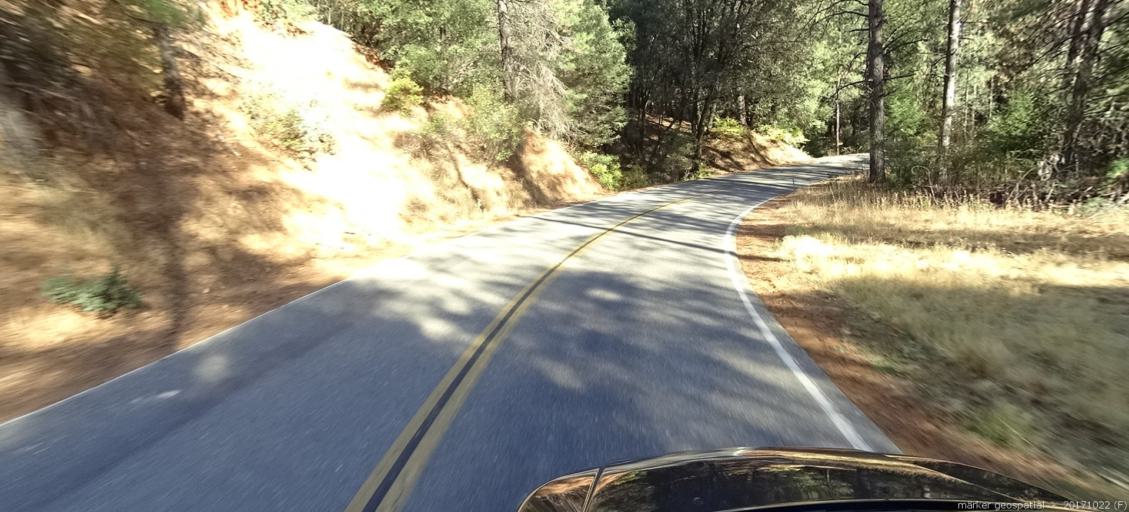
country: US
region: California
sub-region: Shasta County
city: Shasta Lake
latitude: 40.8742
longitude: -122.2540
